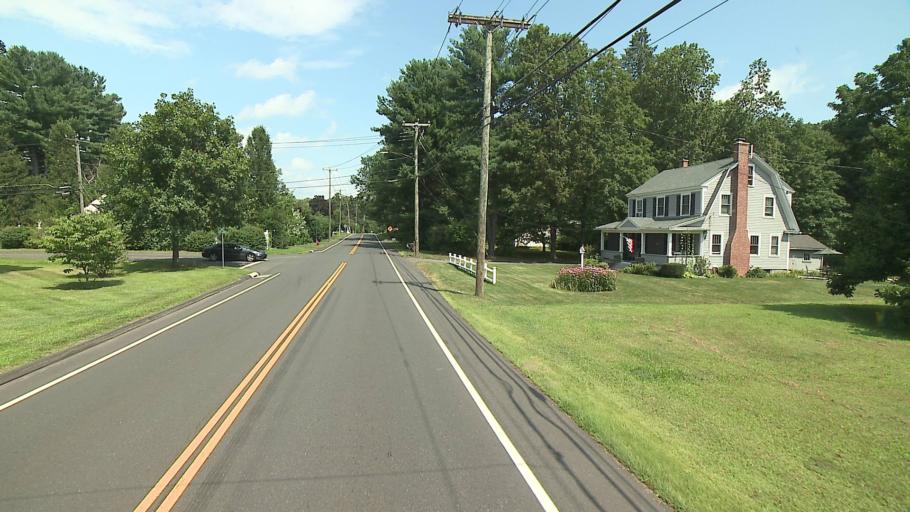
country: US
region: Connecticut
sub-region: Hartford County
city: Collinsville
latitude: 41.7654
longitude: -72.8899
